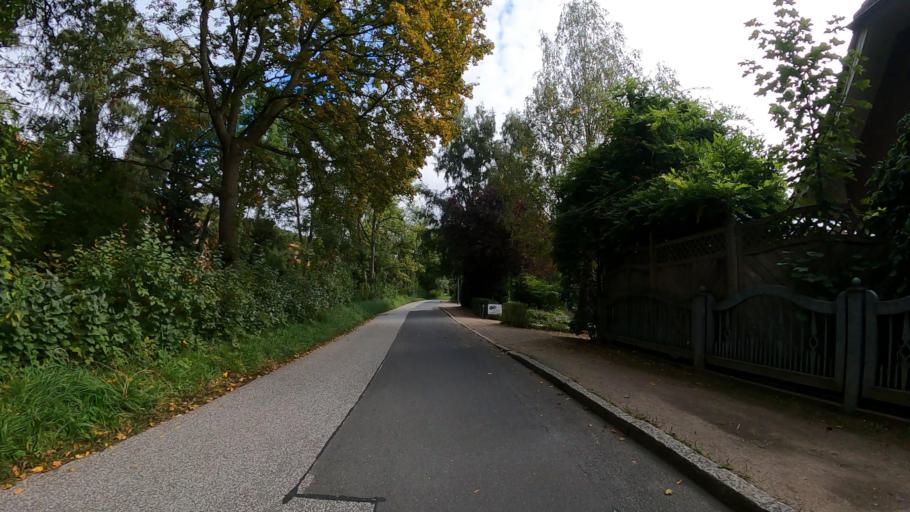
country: DE
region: Hamburg
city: Bergedorf
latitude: 53.4778
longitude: 10.2369
